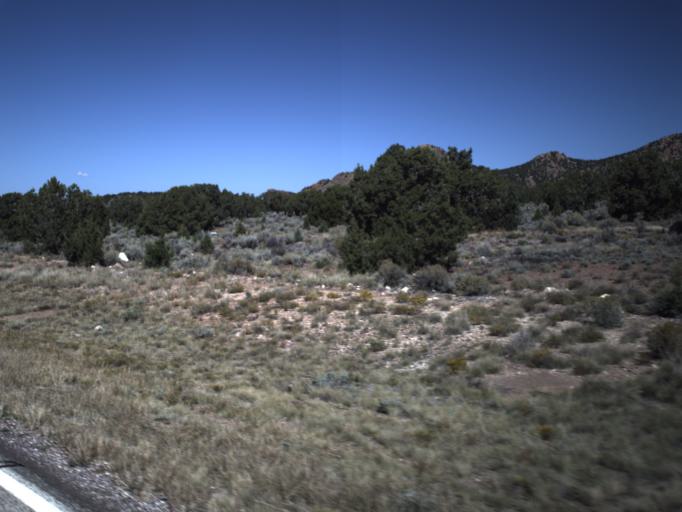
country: US
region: Utah
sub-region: Washington County
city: Enterprise
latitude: 37.6644
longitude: -113.4708
